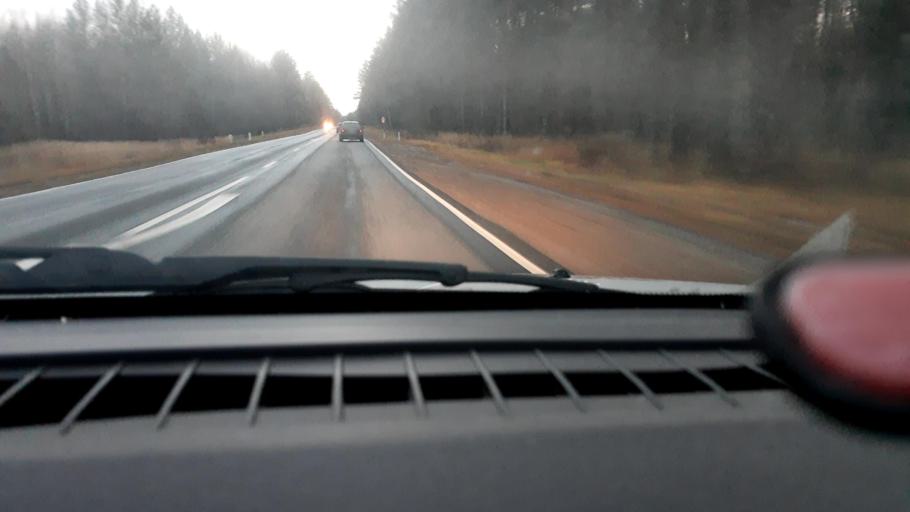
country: RU
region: Nizjnij Novgorod
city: Krasnyye Baki
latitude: 57.0029
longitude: 45.1122
